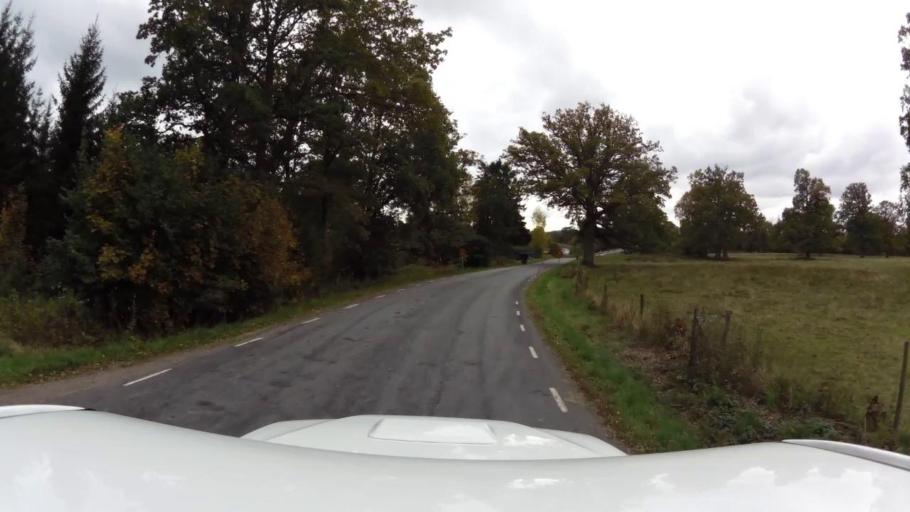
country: SE
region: OEstergoetland
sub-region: Linkopings Kommun
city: Ljungsbro
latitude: 58.5314
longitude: 15.4502
